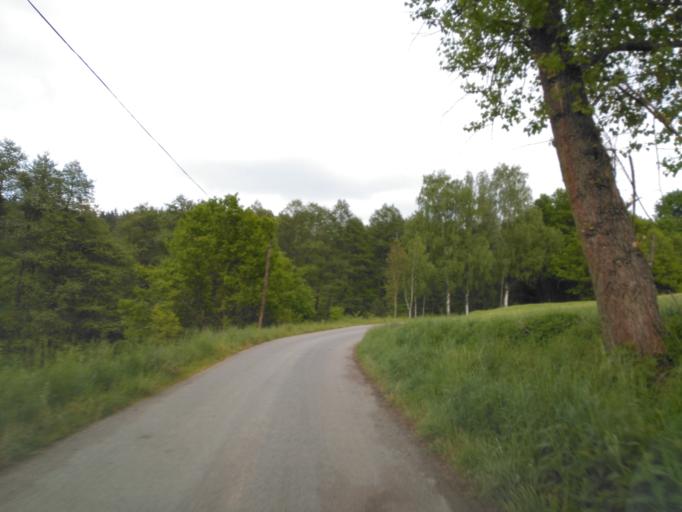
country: CZ
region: Plzensky
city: Zbiroh
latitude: 49.8563
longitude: 13.7287
